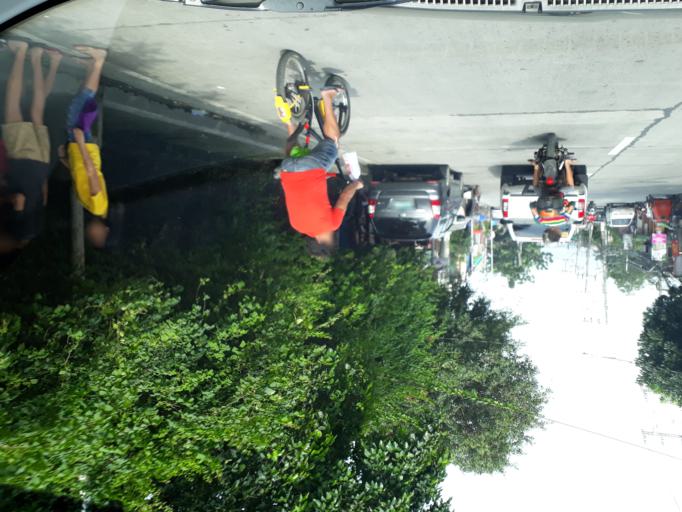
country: PH
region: Calabarzon
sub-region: Province of Rizal
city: Navotas
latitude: 14.6704
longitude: 120.9497
